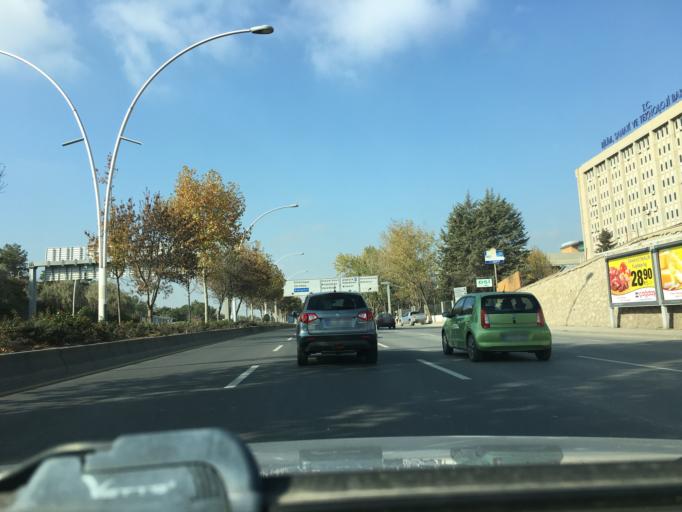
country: TR
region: Ankara
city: Ankara
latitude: 39.9086
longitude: 32.7824
